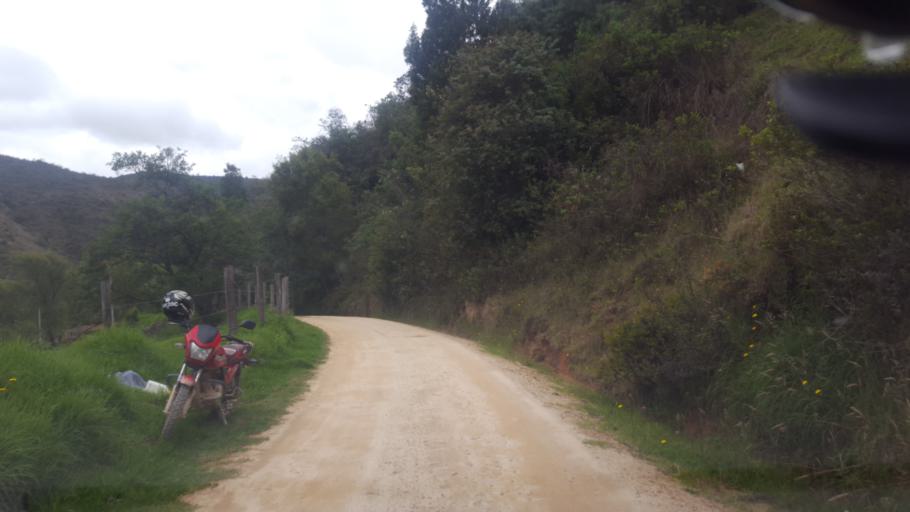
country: CO
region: Boyaca
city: Belen
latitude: 6.0143
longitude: -72.8706
